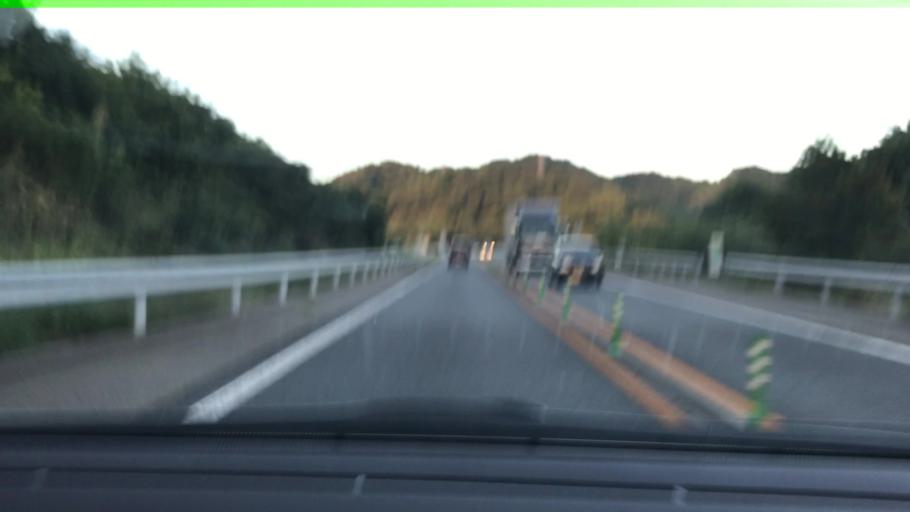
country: JP
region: Hiroshima
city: Innoshima
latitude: 34.3360
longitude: 133.1584
